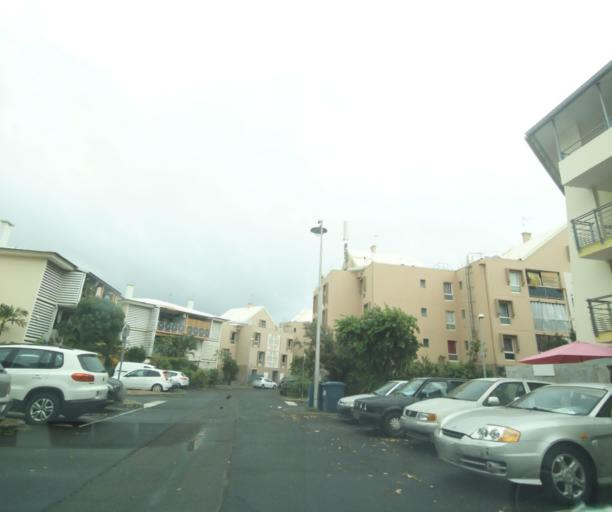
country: RE
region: Reunion
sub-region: Reunion
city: Saint-Paul
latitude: -21.0010
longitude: 55.2800
